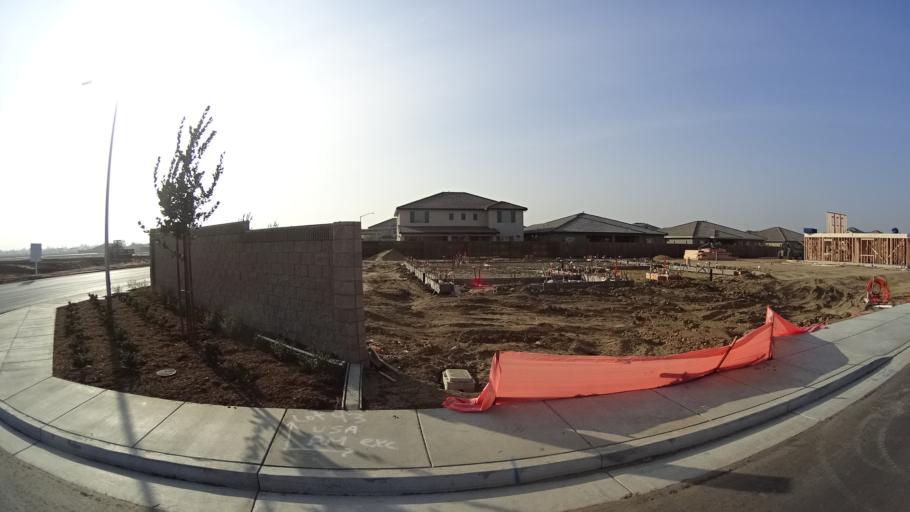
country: US
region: California
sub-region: Kern County
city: Greenacres
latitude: 35.4328
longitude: -119.1014
